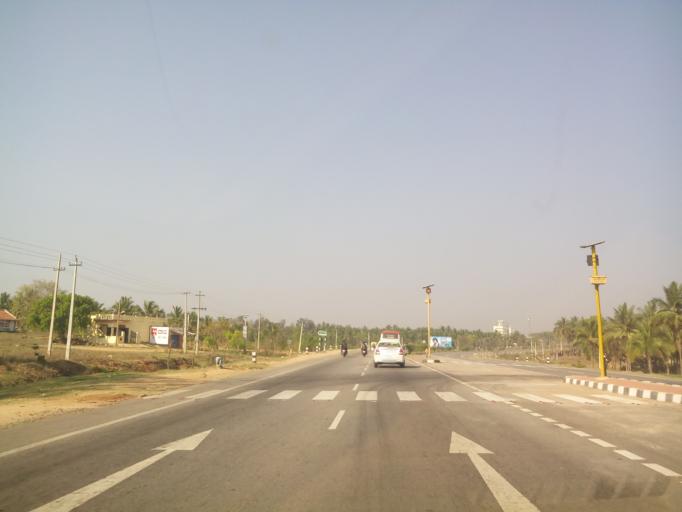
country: IN
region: Karnataka
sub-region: Bangalore Rural
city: Nelamangala
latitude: 13.0635
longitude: 77.3045
